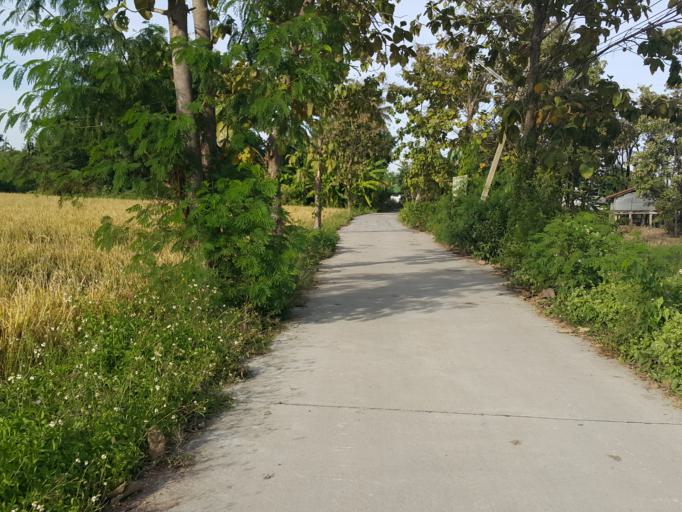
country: TH
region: Chiang Mai
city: San Kamphaeng
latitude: 18.7936
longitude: 99.1238
